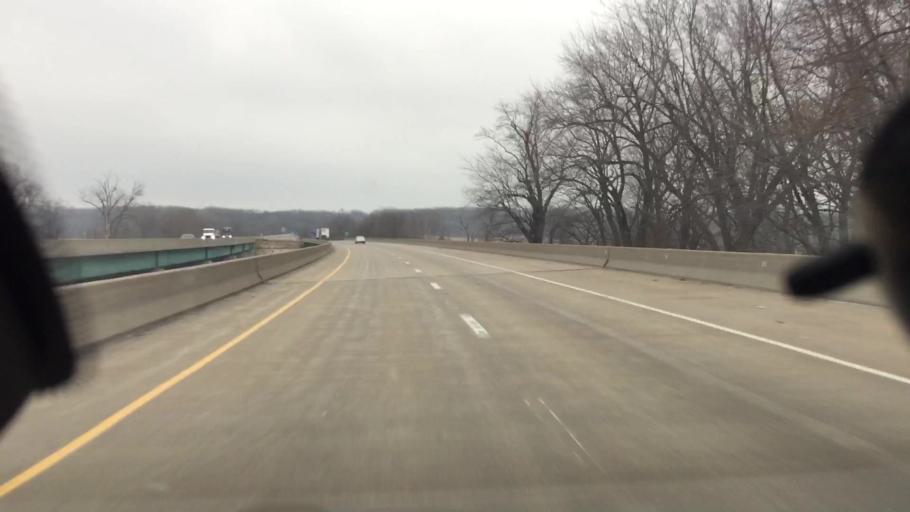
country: US
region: Illinois
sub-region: Henry County
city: Colona
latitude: 41.5125
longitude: -90.3414
